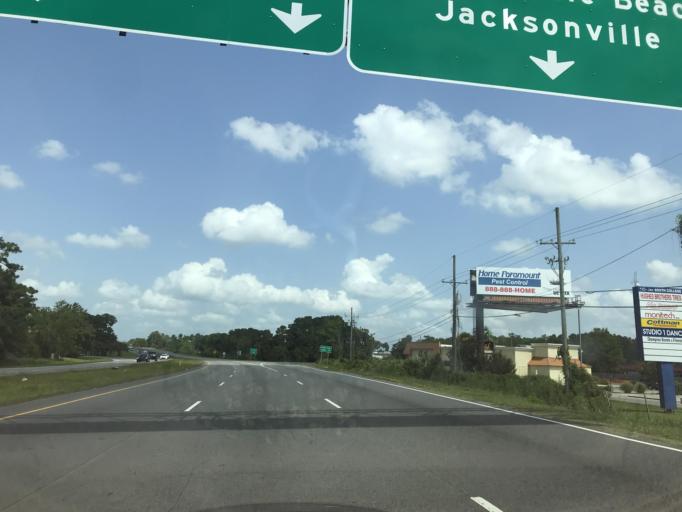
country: US
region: North Carolina
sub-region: New Hanover County
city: Kings Grant
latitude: 34.2403
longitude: -77.8708
